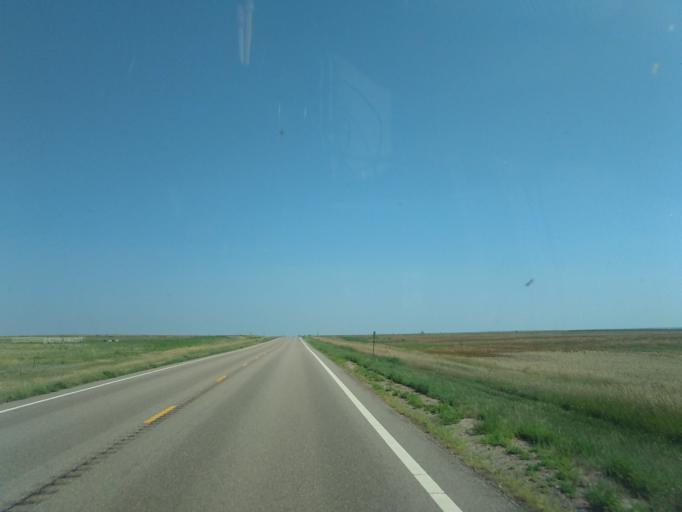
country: US
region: Kansas
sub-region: Cheyenne County
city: Saint Francis
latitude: 39.6525
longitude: -101.7124
